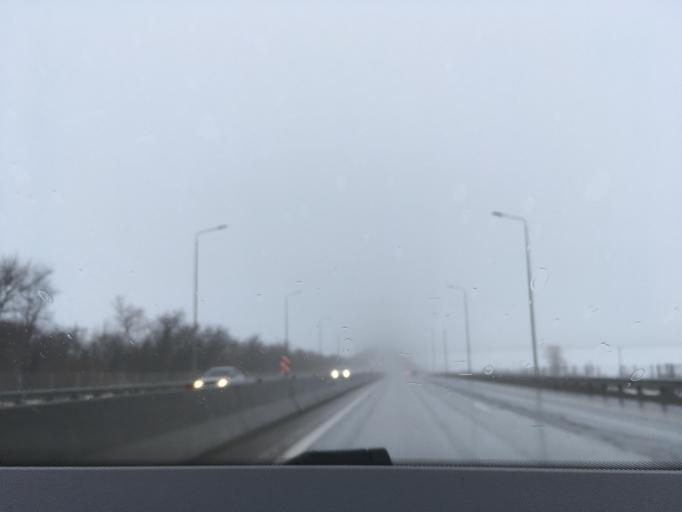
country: RU
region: Rostov
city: Samarskoye
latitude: 46.9575
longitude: 39.7165
